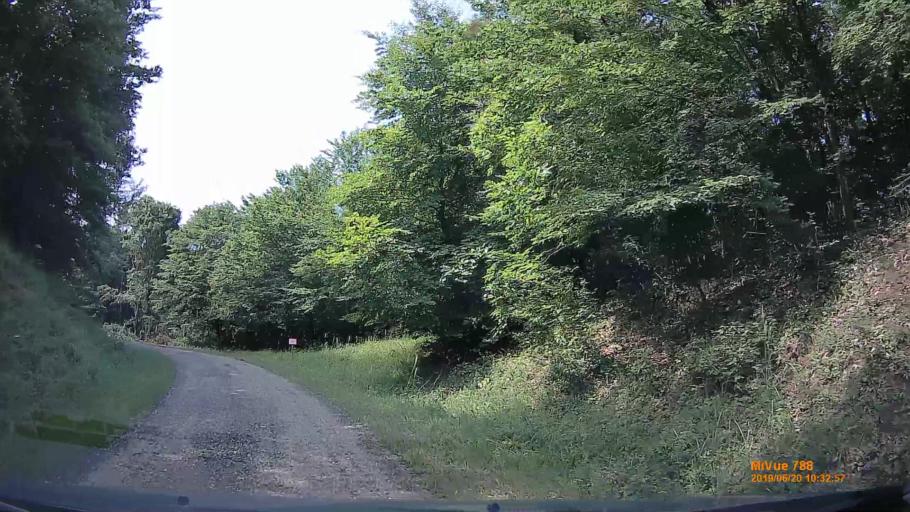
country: HU
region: Baranya
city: Mecseknadasd
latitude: 46.2051
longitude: 18.5155
